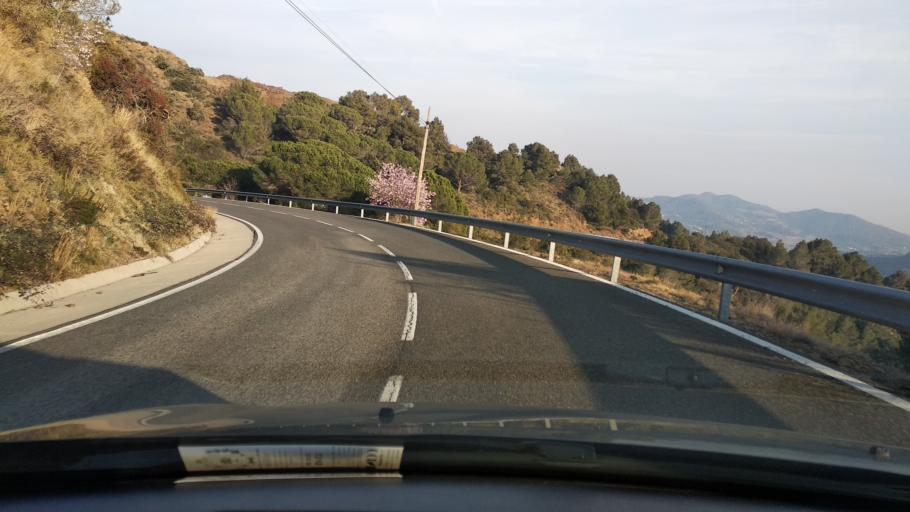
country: ES
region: Catalonia
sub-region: Provincia de Tarragona
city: Alforja
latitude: 41.2183
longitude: 0.9518
